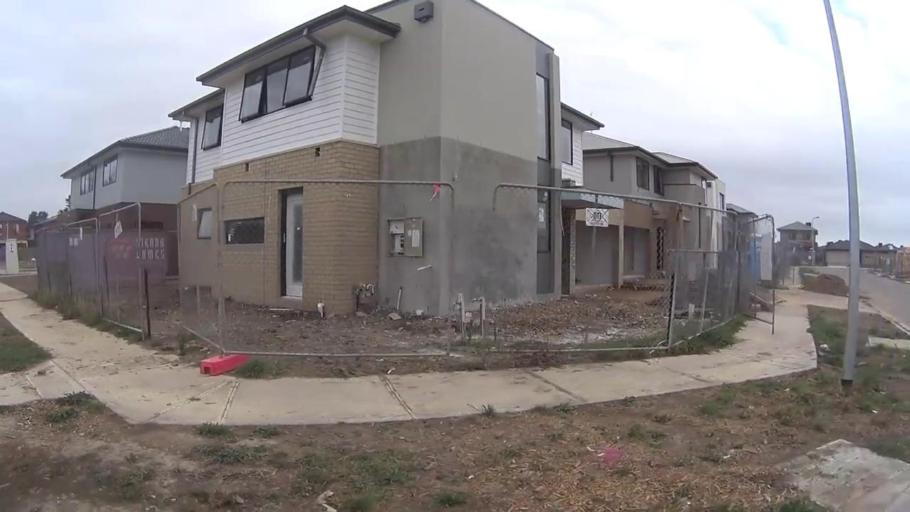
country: AU
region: Victoria
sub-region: Cardinia
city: Officer
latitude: -38.0585
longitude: 145.3986
